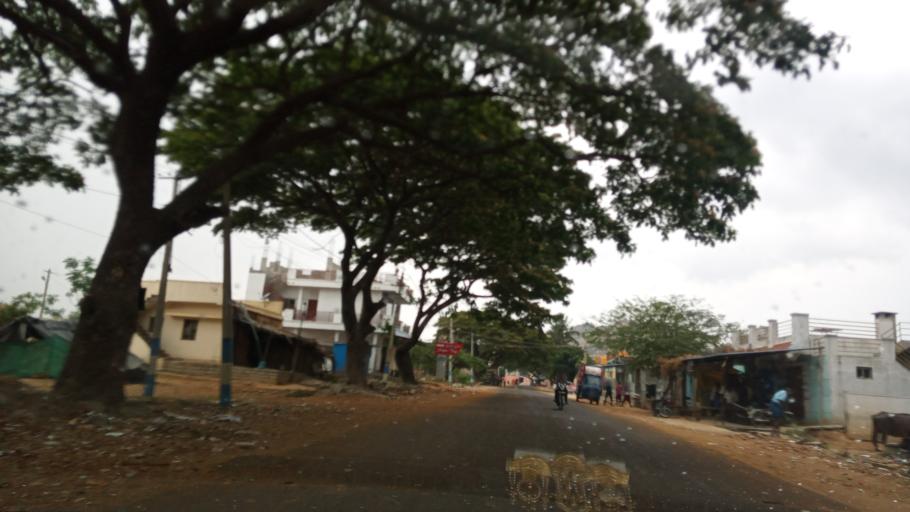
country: IN
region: Karnataka
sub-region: Kolar
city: Mulbagal
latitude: 13.1078
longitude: 78.3350
